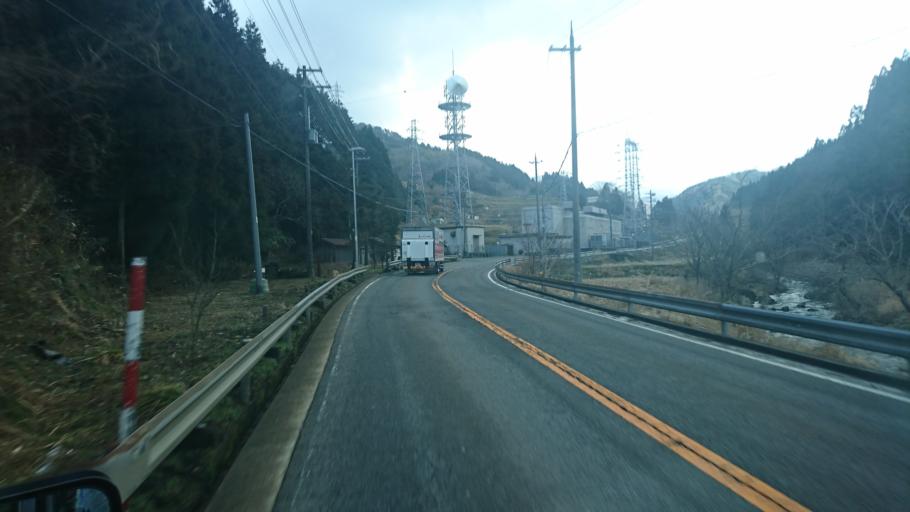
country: JP
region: Tottori
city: Tottori
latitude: 35.5434
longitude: 134.5056
